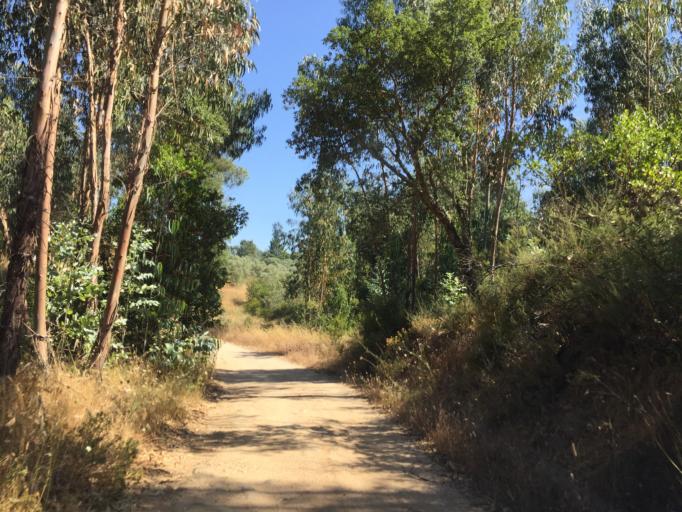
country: PT
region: Santarem
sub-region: Tomar
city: Tomar
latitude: 39.6101
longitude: -8.3490
